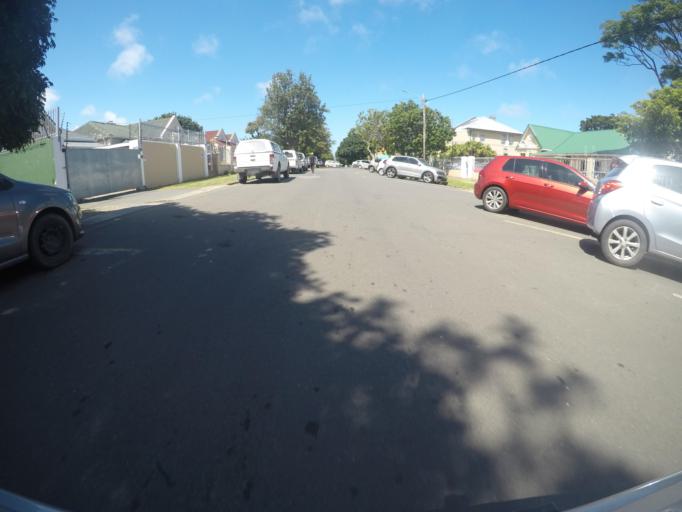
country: ZA
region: Eastern Cape
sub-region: Buffalo City Metropolitan Municipality
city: East London
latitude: -33.0028
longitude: 27.8965
